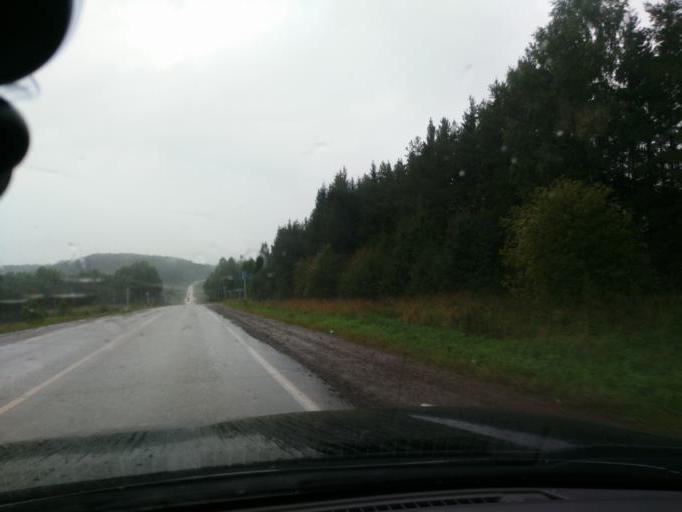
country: RU
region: Perm
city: Osa
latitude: 57.2932
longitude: 55.6107
